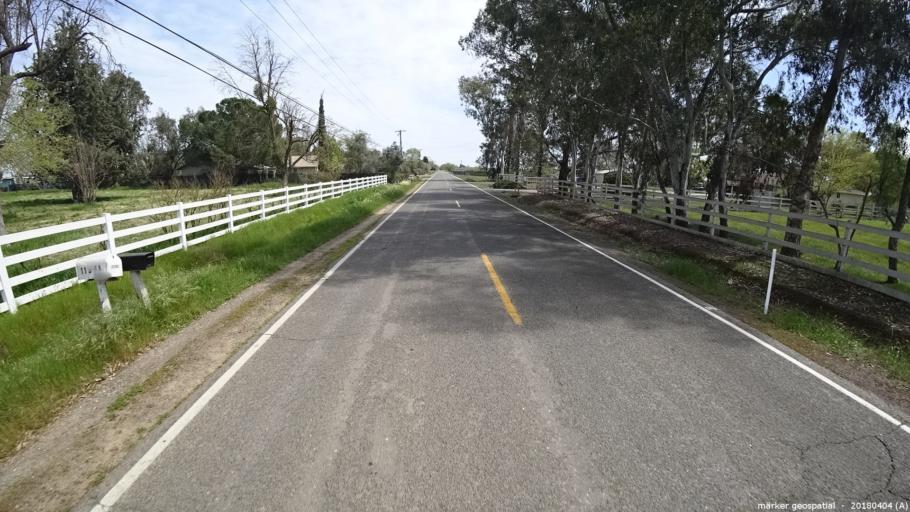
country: US
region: California
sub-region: Sacramento County
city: Herald
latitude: 38.2626
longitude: -121.2616
